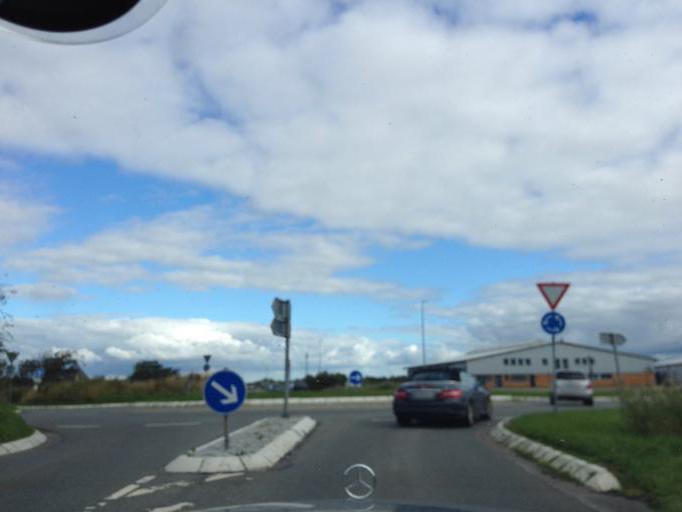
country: DE
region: Schleswig-Holstein
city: Dagebull
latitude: 54.7328
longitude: 8.7014
